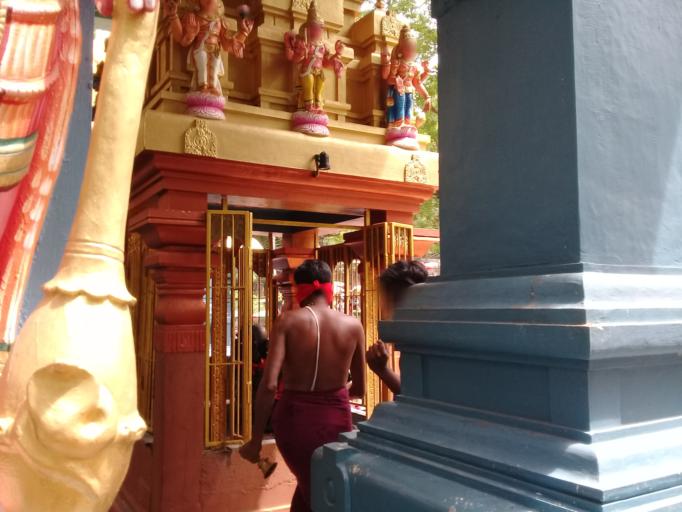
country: LK
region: Uva
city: Wattegama
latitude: 6.4366
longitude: 81.3023
